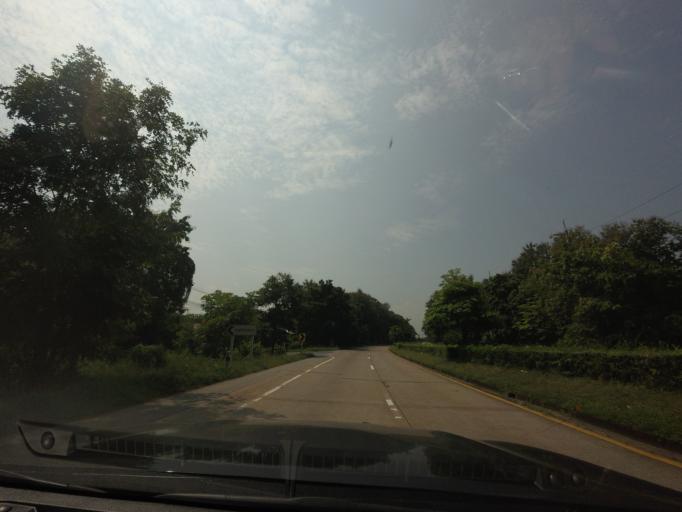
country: TH
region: Phrae
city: Sung Men
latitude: 17.9995
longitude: 100.1028
